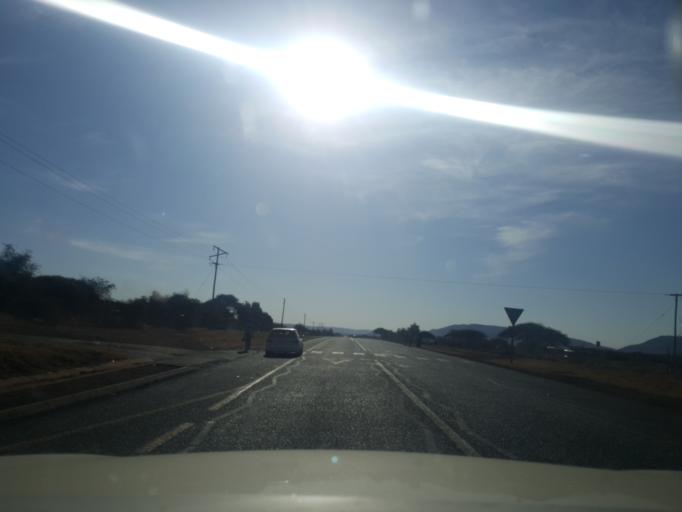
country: ZA
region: North-West
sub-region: Ngaka Modiri Molema District Municipality
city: Zeerust
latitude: -25.4784
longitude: 25.9073
